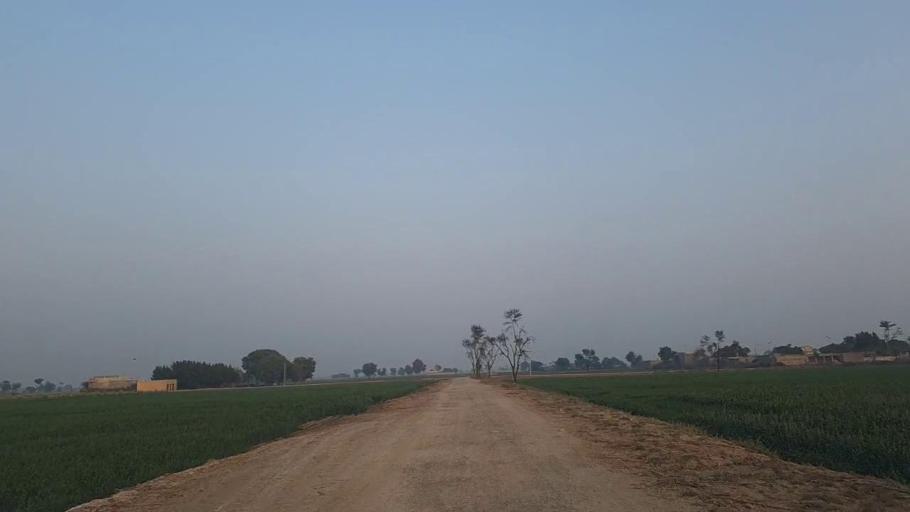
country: PK
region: Sindh
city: Nawabshah
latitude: 26.2601
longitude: 68.4549
